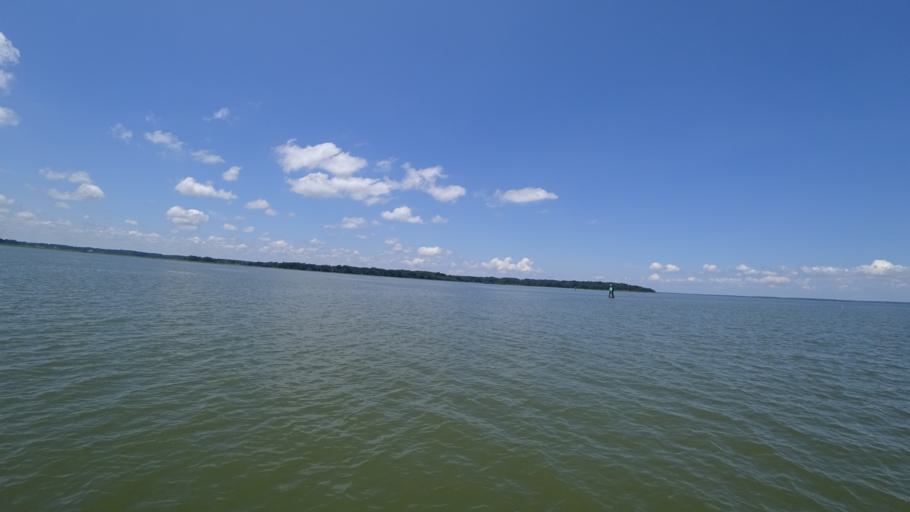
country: US
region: Virginia
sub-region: Isle of Wight County
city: Carrollton
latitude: 37.0022
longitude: -76.5726
